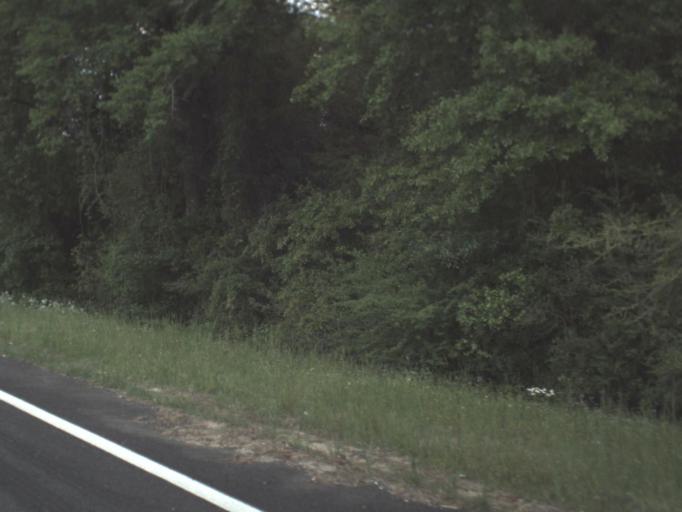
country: US
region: Florida
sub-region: Escambia County
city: Century
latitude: 30.8573
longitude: -87.3230
